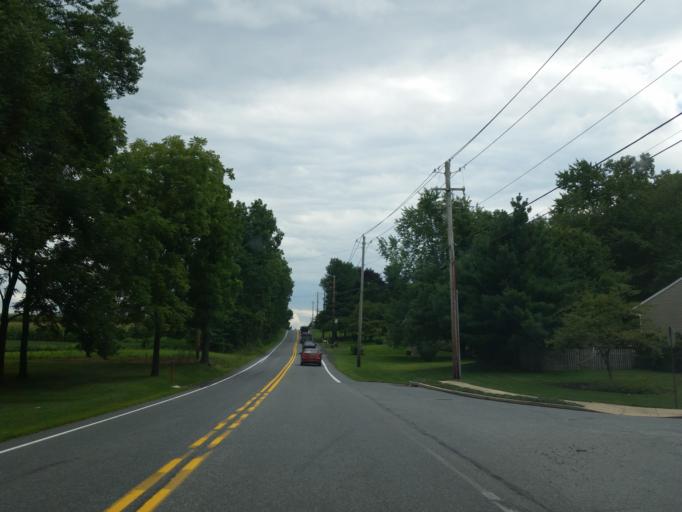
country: US
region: Pennsylvania
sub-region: Lancaster County
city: Swartzville
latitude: 40.2374
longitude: -76.0810
